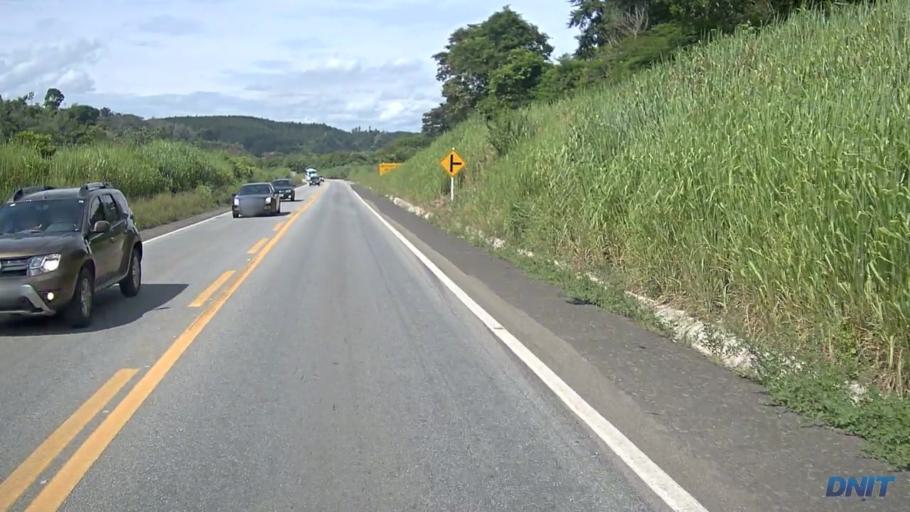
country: BR
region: Minas Gerais
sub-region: Ipaba
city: Ipaba
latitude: -19.3911
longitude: -42.4794
